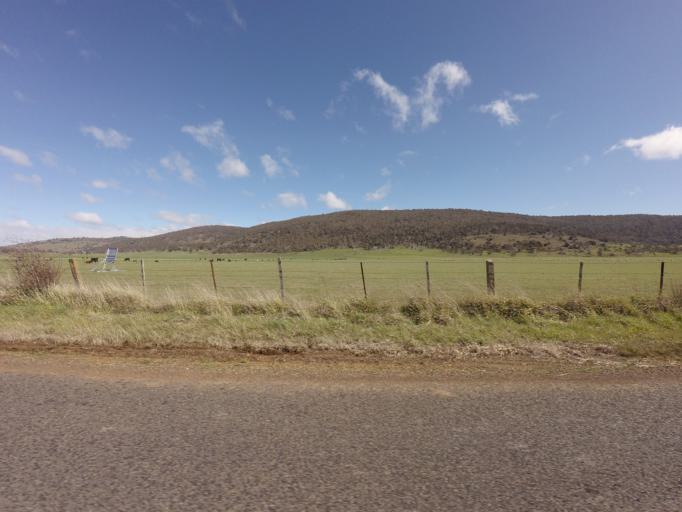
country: AU
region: Tasmania
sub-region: Northern Midlands
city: Evandale
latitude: -41.9736
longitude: 147.4446
